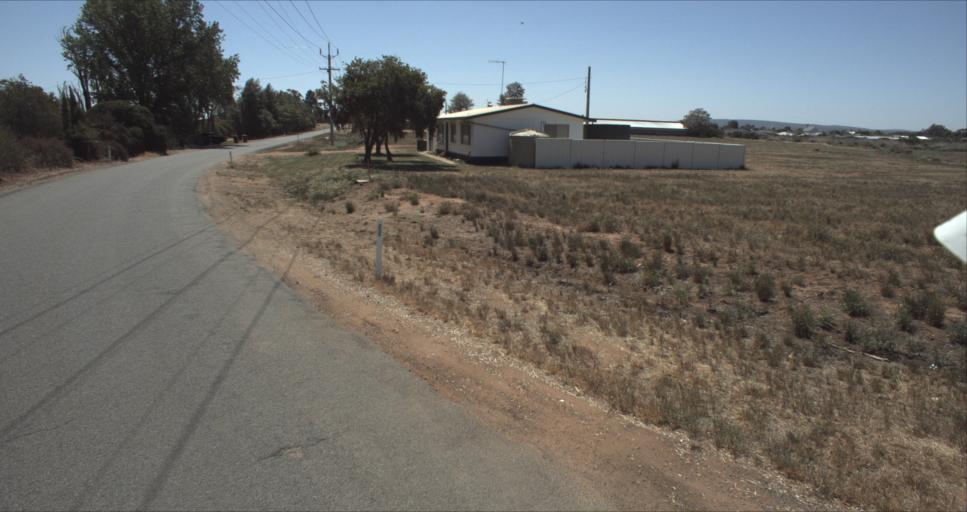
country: AU
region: New South Wales
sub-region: Leeton
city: Leeton
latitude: -34.5428
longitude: 146.3943
